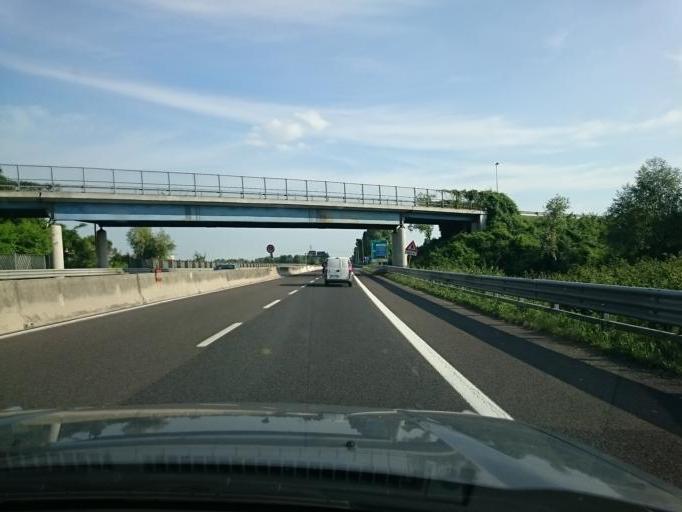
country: IT
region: Veneto
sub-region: Provincia di Padova
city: Mandriola-Sant'Agostino
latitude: 45.3697
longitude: 11.8545
